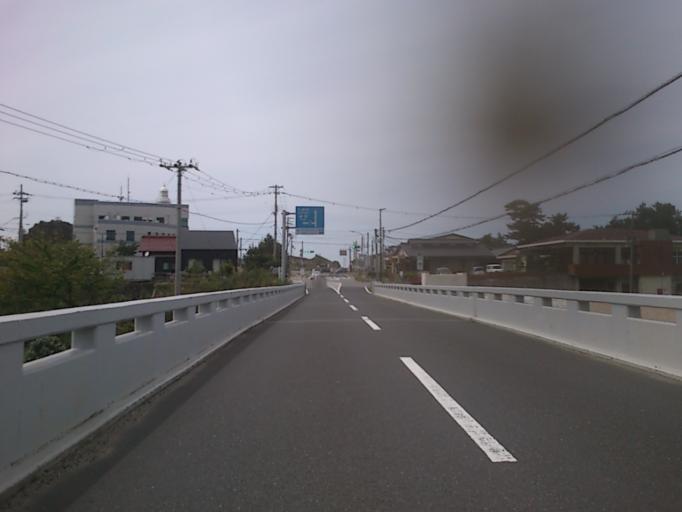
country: JP
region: Kyoto
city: Miyazu
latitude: 35.7391
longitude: 135.1037
